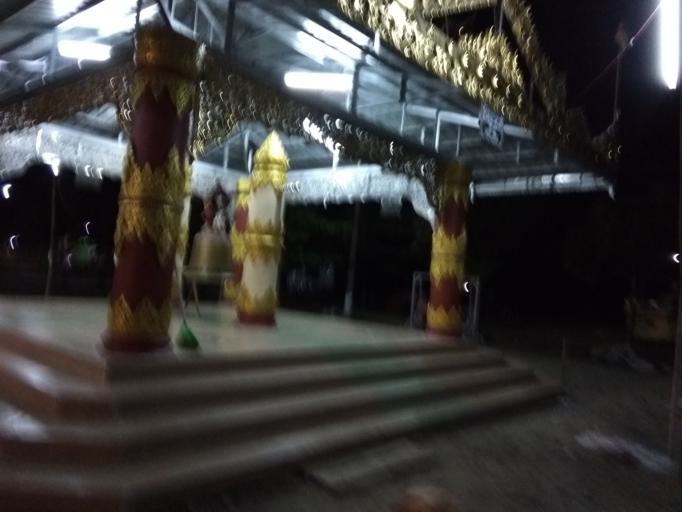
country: MM
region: Ayeyarwady
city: Mawlamyinegyunn
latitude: 16.3743
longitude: 95.2699
